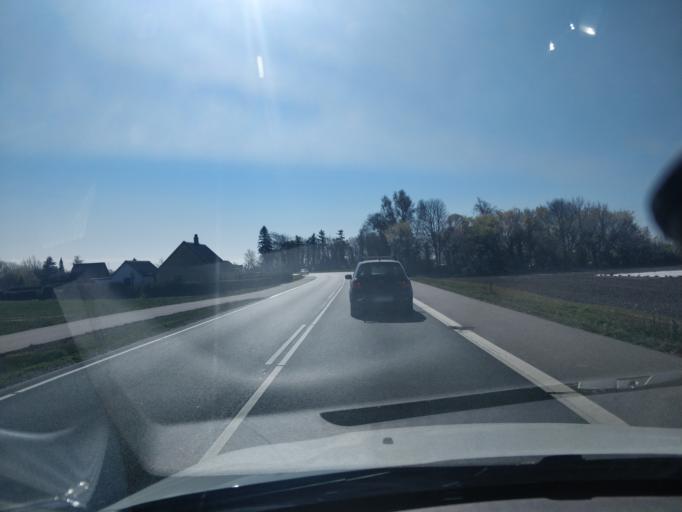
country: DK
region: Zealand
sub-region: Vordingborg Kommune
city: Stege
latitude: 54.9685
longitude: 12.2007
